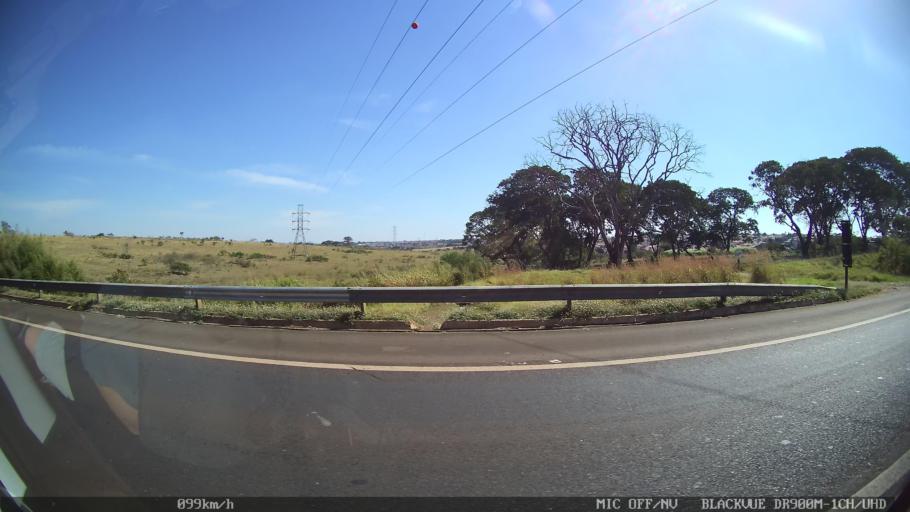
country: BR
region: Sao Paulo
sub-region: Franca
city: Franca
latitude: -20.5194
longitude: -47.4178
